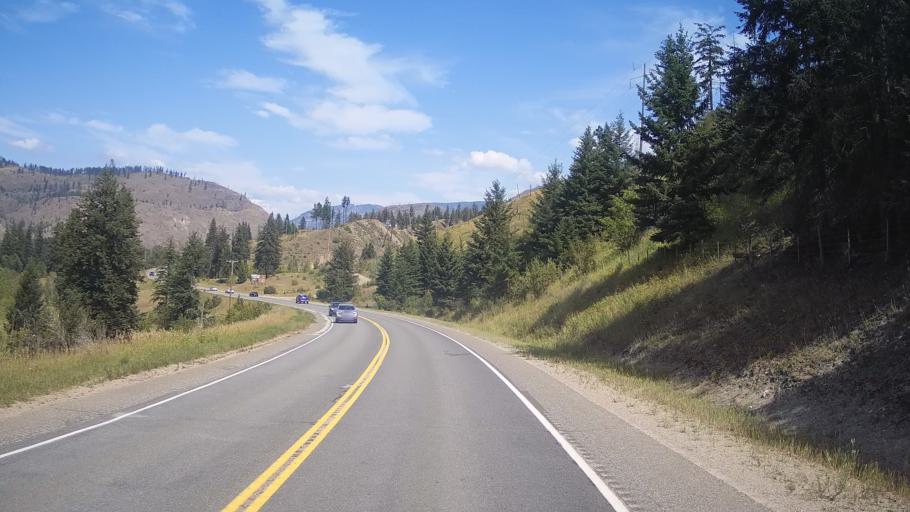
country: CA
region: British Columbia
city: Kamloops
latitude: 51.0877
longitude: -120.1773
